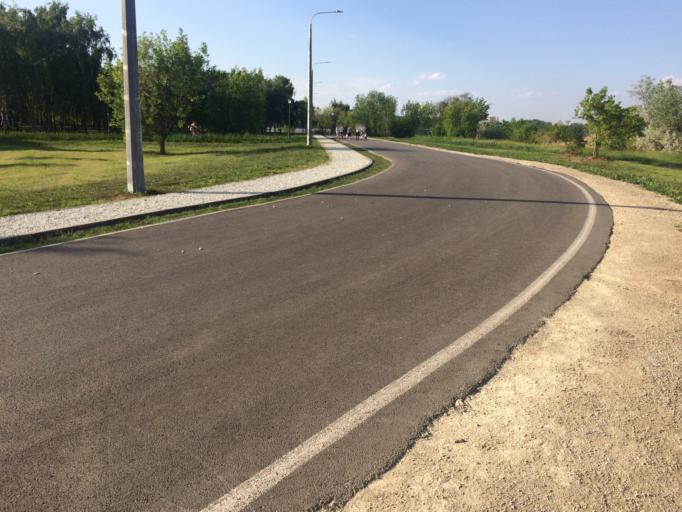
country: RU
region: Chelyabinsk
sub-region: Gorod Magnitogorsk
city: Magnitogorsk
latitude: 53.4015
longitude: 58.9946
